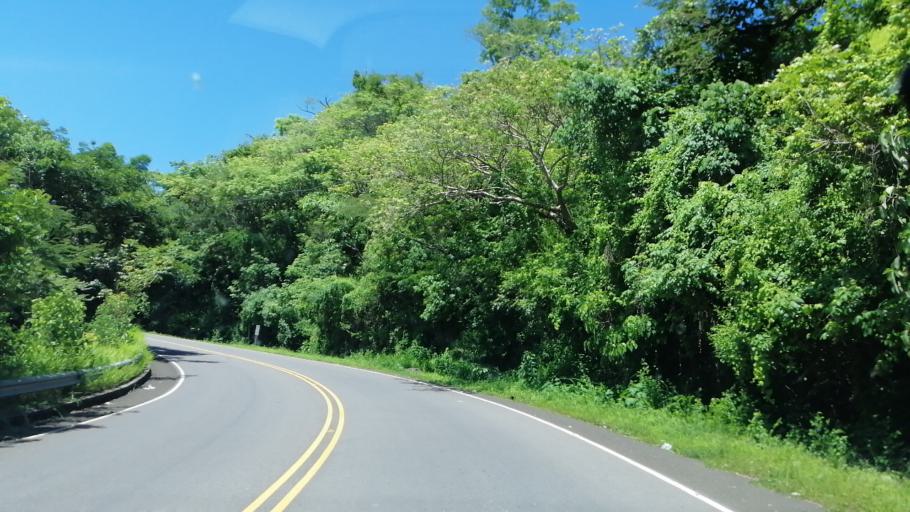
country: SV
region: San Miguel
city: Ciudad Barrios
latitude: 13.8122
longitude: -88.1767
